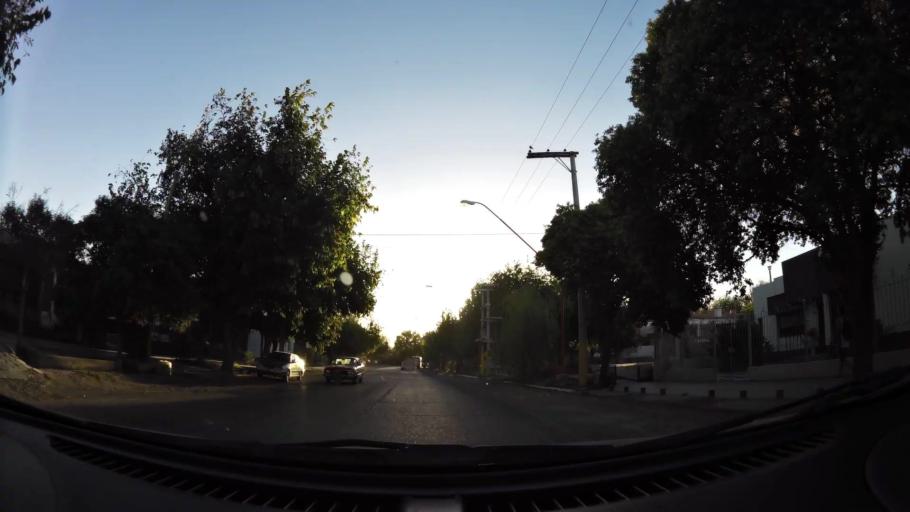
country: AR
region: San Juan
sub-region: Departamento de Santa Lucia
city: Santa Lucia
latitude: -31.5334
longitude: -68.4961
